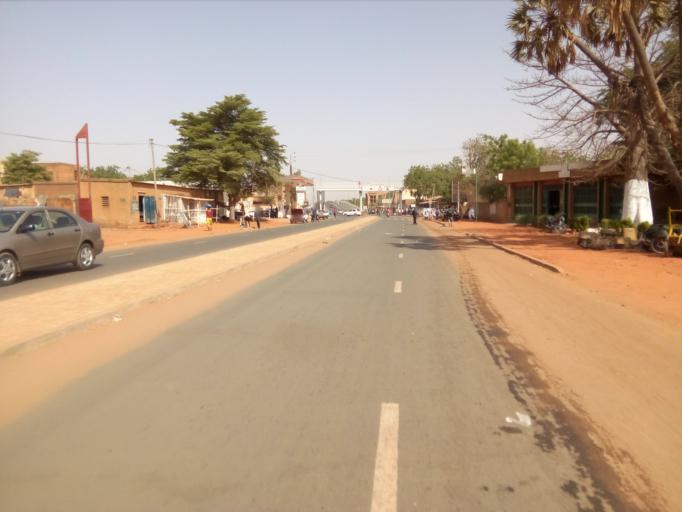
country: NE
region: Niamey
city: Niamey
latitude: 13.5198
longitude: 2.1227
